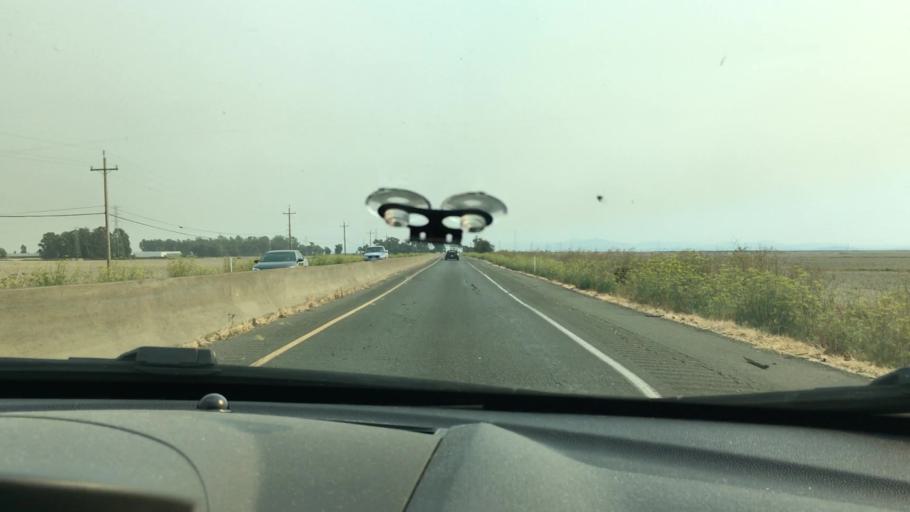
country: US
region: California
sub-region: Marin County
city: Black Point-Green Point
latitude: 38.1535
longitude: -122.4356
